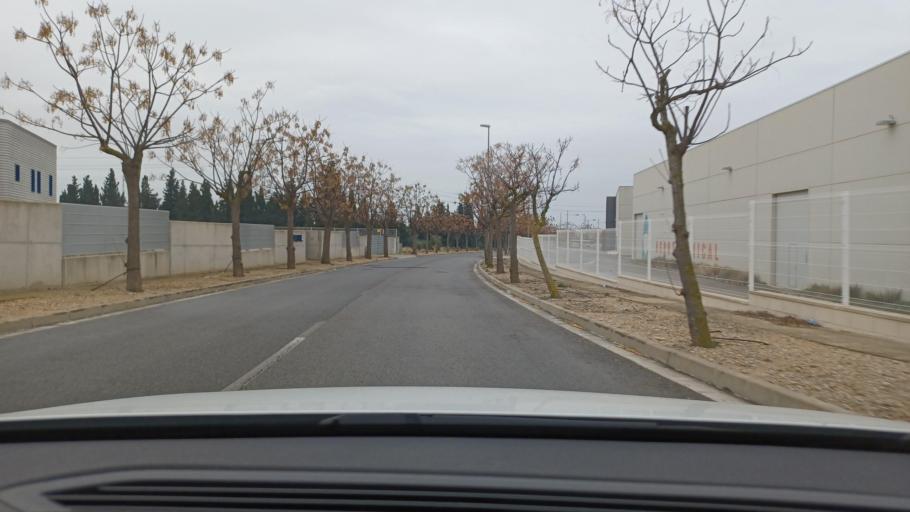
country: ES
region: Catalonia
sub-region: Provincia de Tarragona
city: Amposta
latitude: 40.7576
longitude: 0.6005
